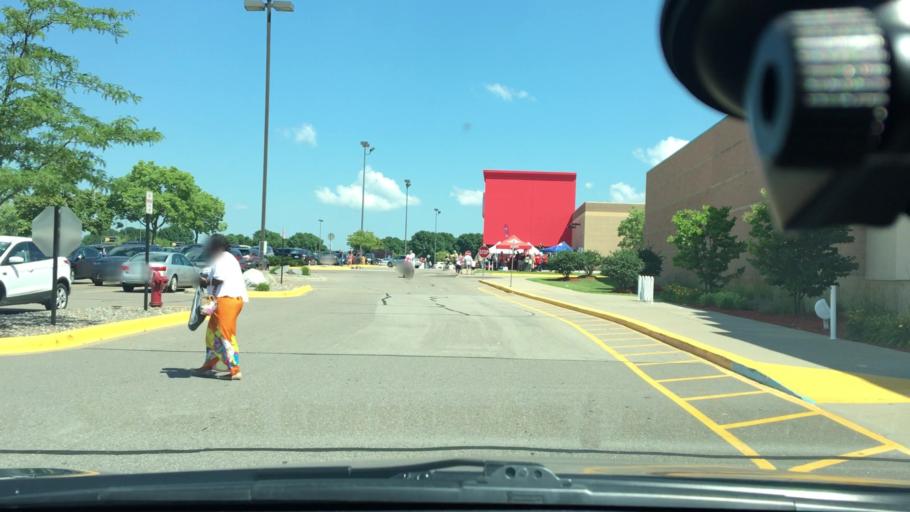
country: US
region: Minnesota
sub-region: Hennepin County
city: Maple Grove
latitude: 45.1014
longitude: -93.4483
